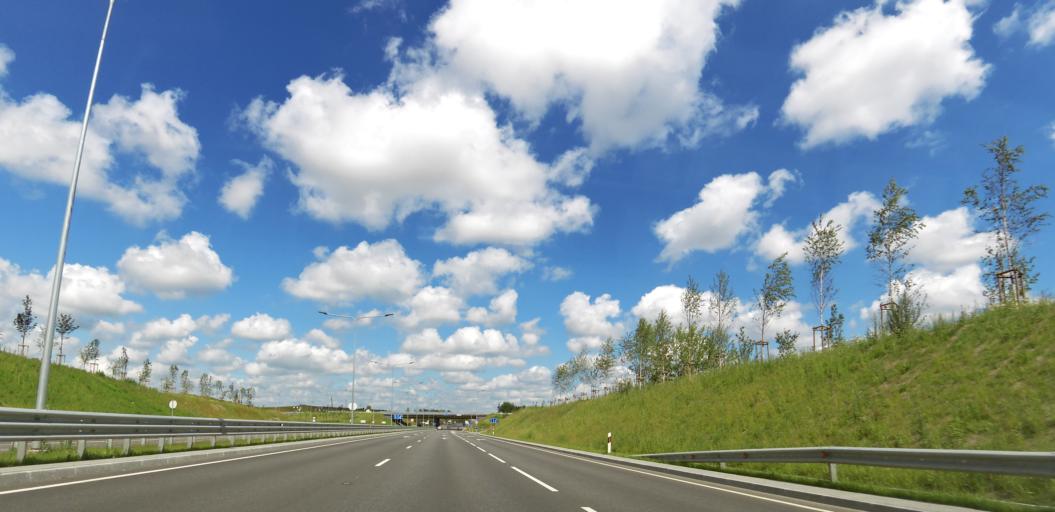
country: LT
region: Vilnius County
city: Justiniskes
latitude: 54.7221
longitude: 25.2081
